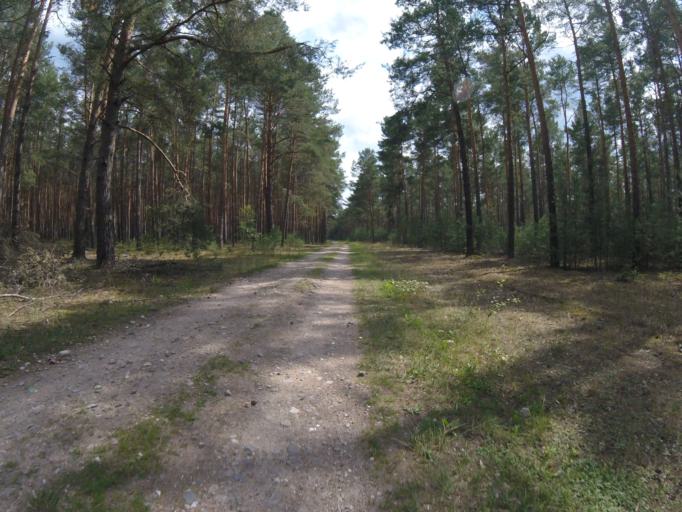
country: DE
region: Brandenburg
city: Halbe
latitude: 52.1227
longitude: 13.6971
